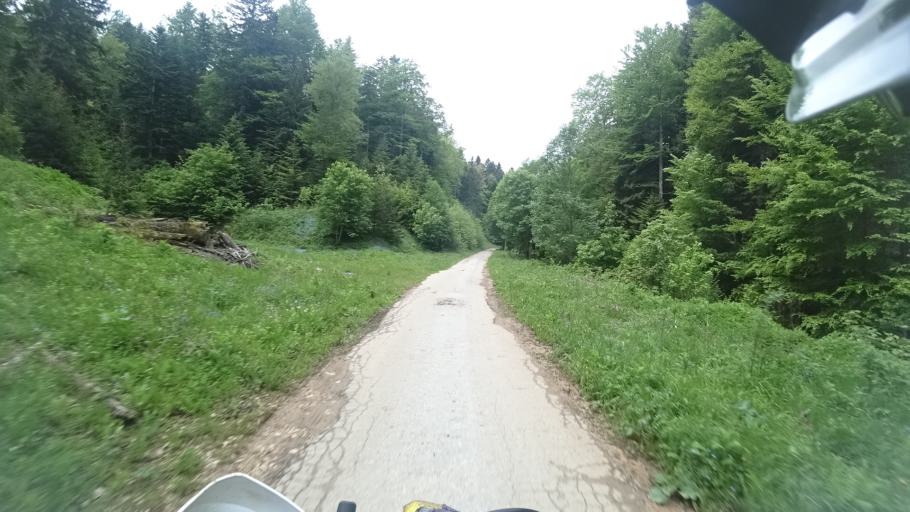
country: BA
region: Federation of Bosnia and Herzegovina
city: Bihac
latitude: 44.6737
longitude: 15.8498
